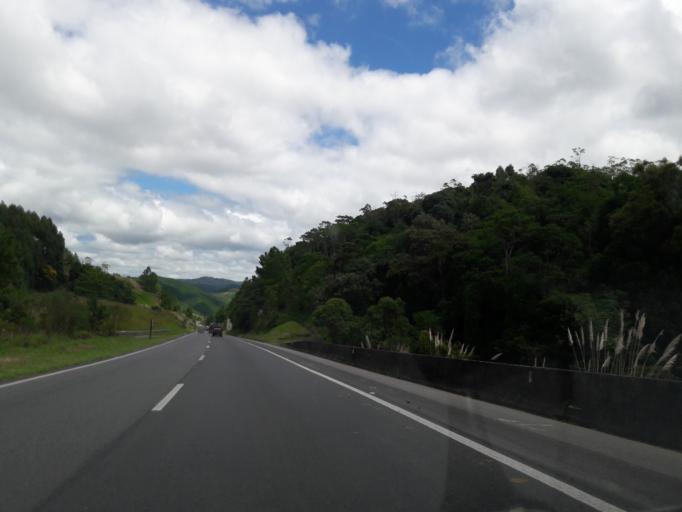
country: BR
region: Parana
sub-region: Campina Grande Do Sul
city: Campina Grande do Sul
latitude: -25.0996
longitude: -48.8144
